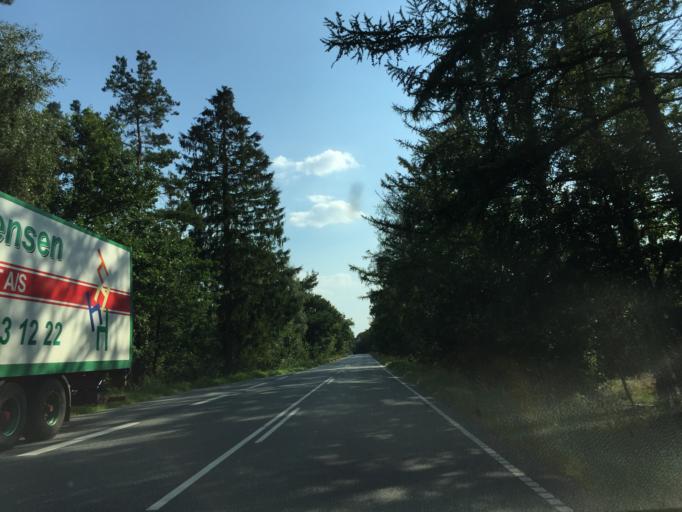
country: DK
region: Central Jutland
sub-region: Viborg Kommune
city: Bjerringbro
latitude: 56.3048
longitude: 9.6856
